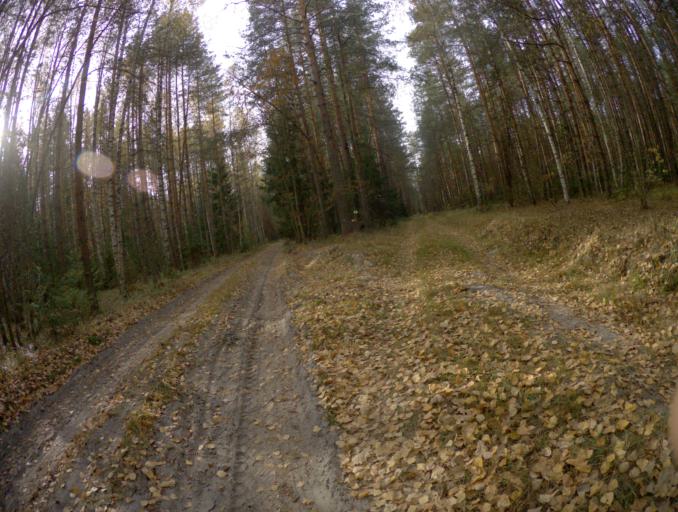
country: RU
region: Vladimir
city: Vorsha
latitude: 55.9521
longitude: 40.1377
